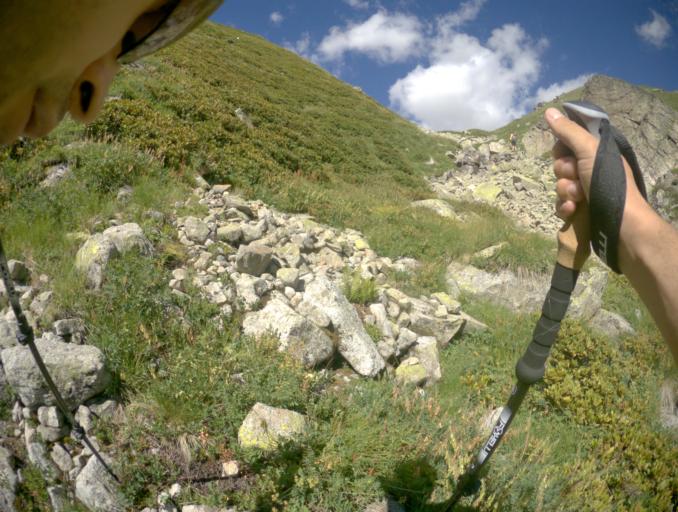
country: RU
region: Karachayevo-Cherkesiya
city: Uchkulan
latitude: 43.3254
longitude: 42.1068
